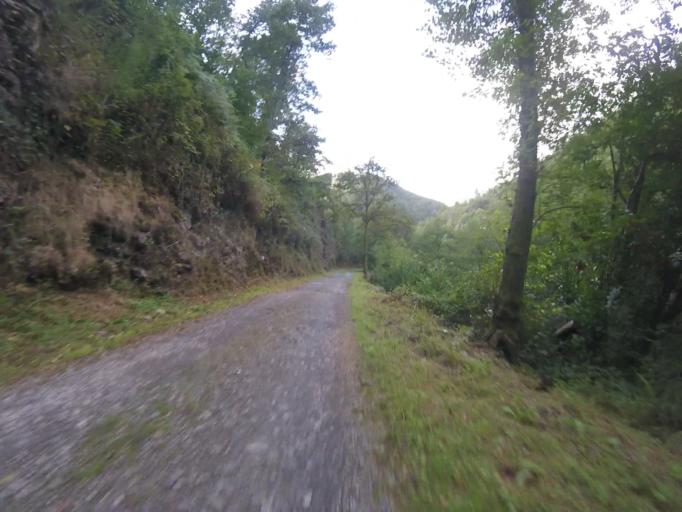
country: ES
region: Basque Country
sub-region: Provincia de Guipuzcoa
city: Berastegui
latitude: 43.1516
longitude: -1.9642
